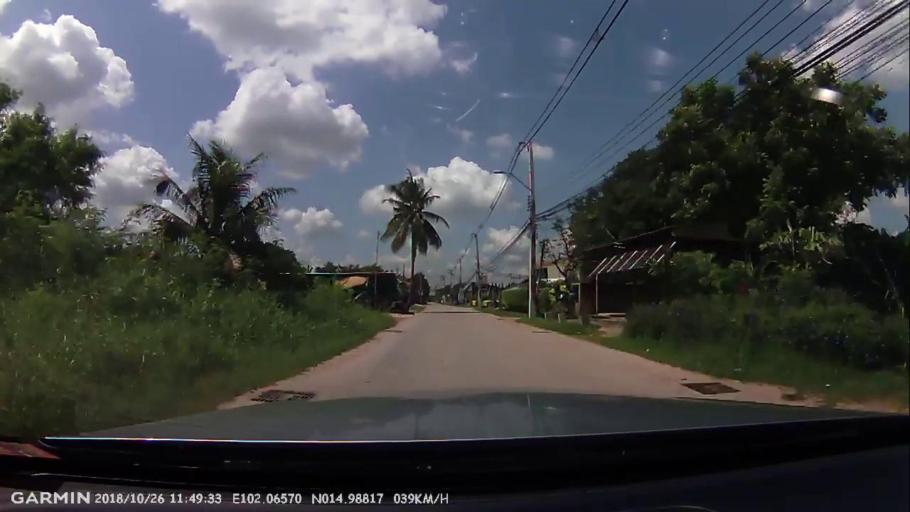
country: TH
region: Nakhon Ratchasima
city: Nakhon Ratchasima
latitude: 14.9882
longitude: 102.0655
